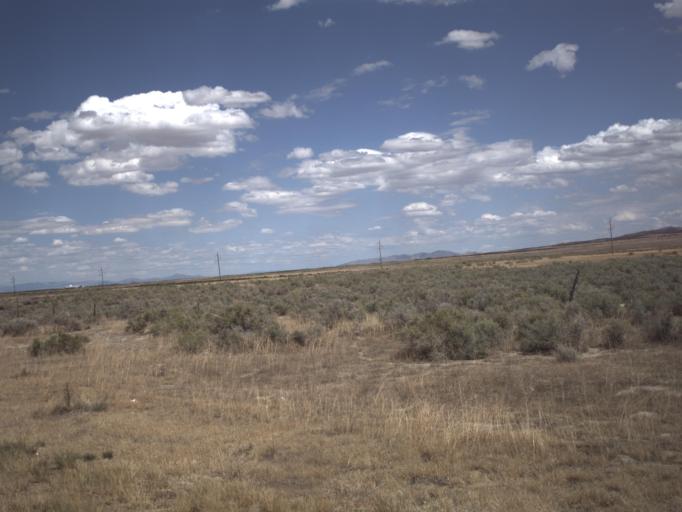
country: US
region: Utah
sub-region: Millard County
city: Delta
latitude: 39.2522
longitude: -112.4404
